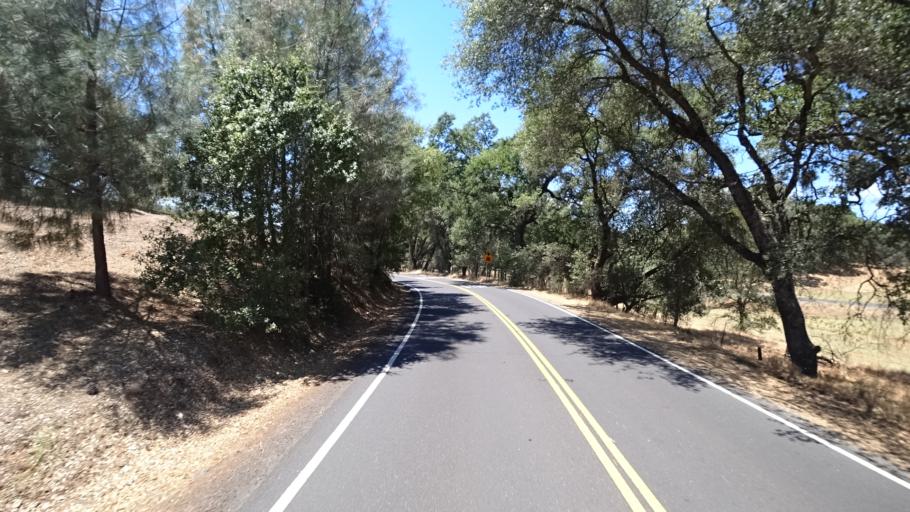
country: US
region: California
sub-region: Calaveras County
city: Angels Camp
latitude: 38.0772
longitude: -120.5625
